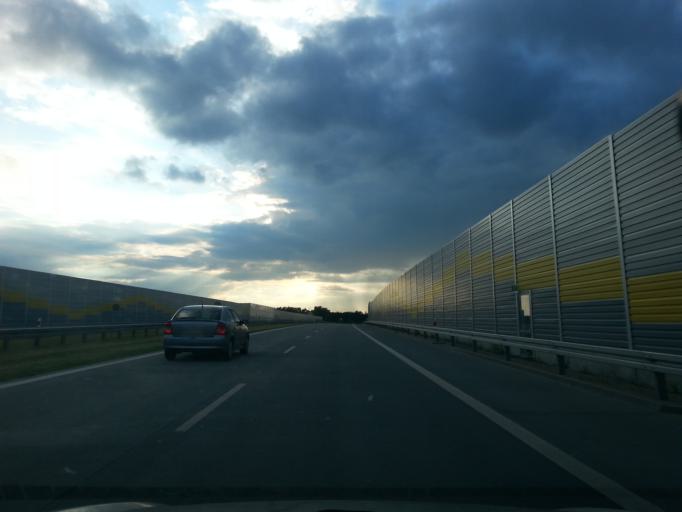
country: PL
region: Lodz Voivodeship
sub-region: Powiat zdunskowolski
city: Zdunska Wola
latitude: 51.5793
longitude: 18.9133
